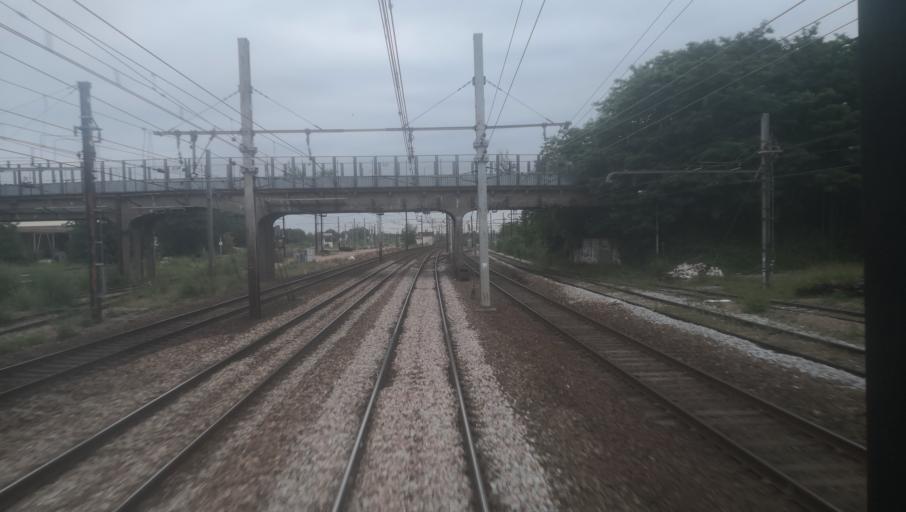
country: FR
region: Ile-de-France
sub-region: Departement de l'Essonne
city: Marolles-en-Hurepoix
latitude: 48.5860
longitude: 2.2913
